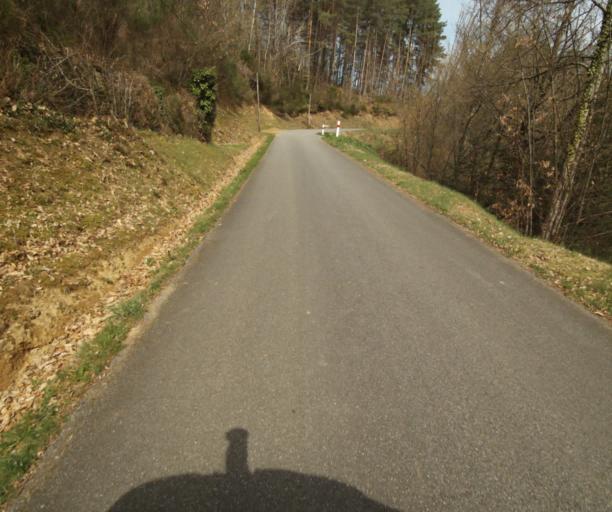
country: FR
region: Limousin
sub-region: Departement de la Correze
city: Naves
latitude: 45.3254
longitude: 1.8059
